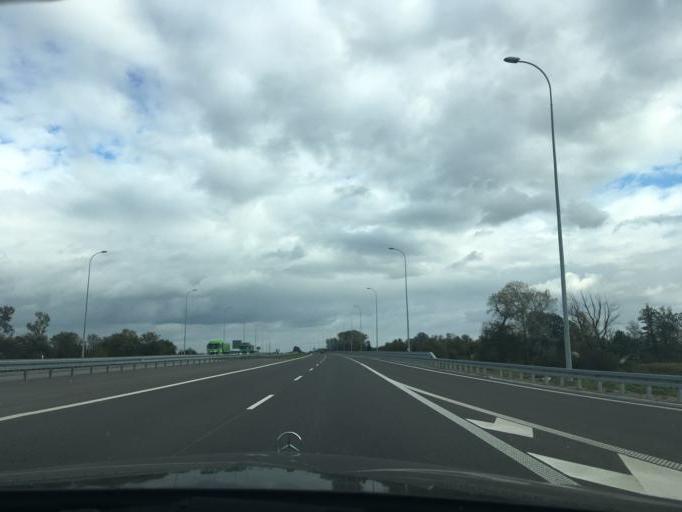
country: PL
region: Subcarpathian Voivodeship
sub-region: Powiat lancucki
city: Czarna
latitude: 50.0899
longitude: 22.1779
